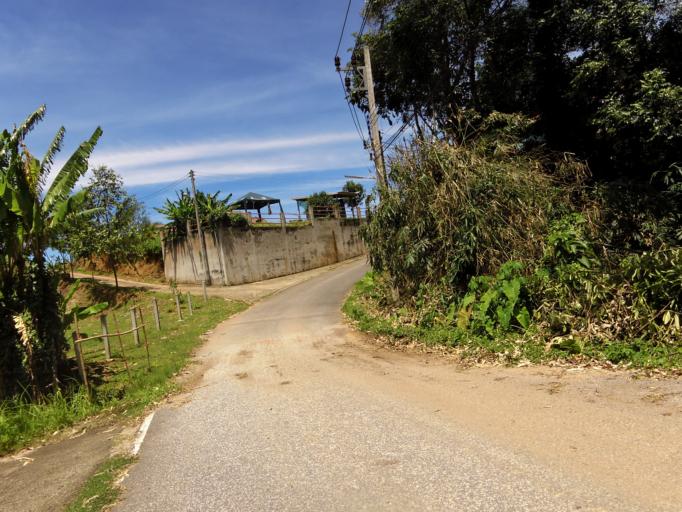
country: TH
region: Phuket
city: Ban Karon
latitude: 7.8500
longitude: 98.3071
